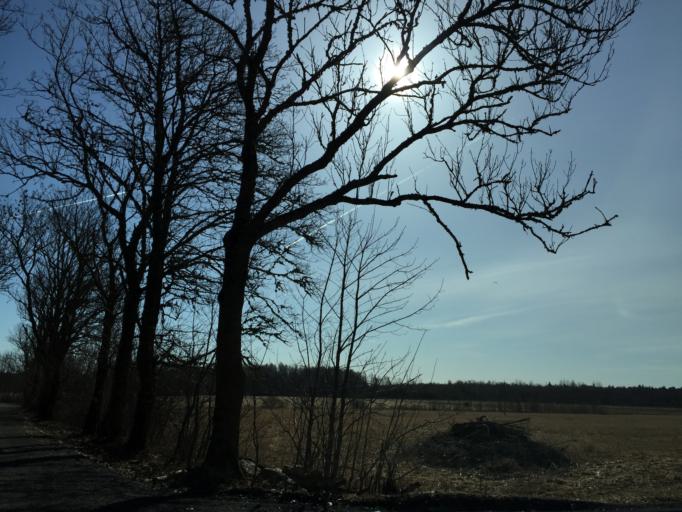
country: EE
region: Laeaene
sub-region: Ridala Parish
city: Uuemoisa
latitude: 58.6746
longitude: 23.5476
